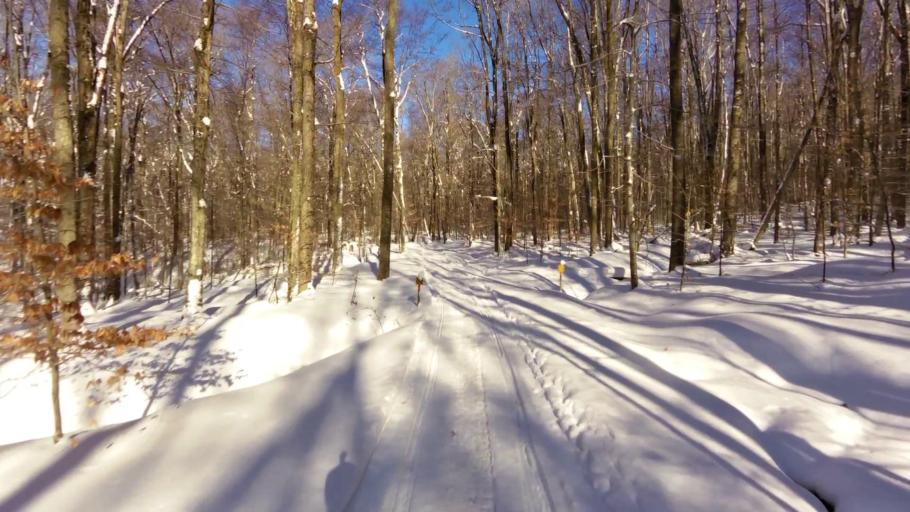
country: US
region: New York
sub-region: Cattaraugus County
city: Salamanca
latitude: 42.0357
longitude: -78.7789
